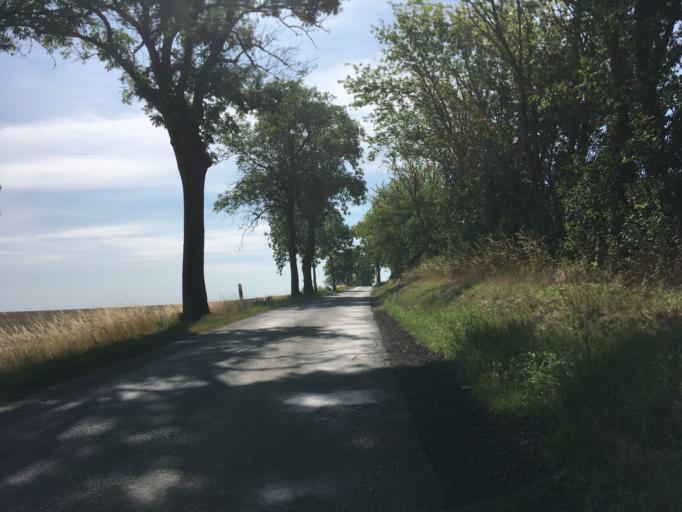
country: DE
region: Brandenburg
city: Gramzow
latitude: 53.2828
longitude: 14.0549
